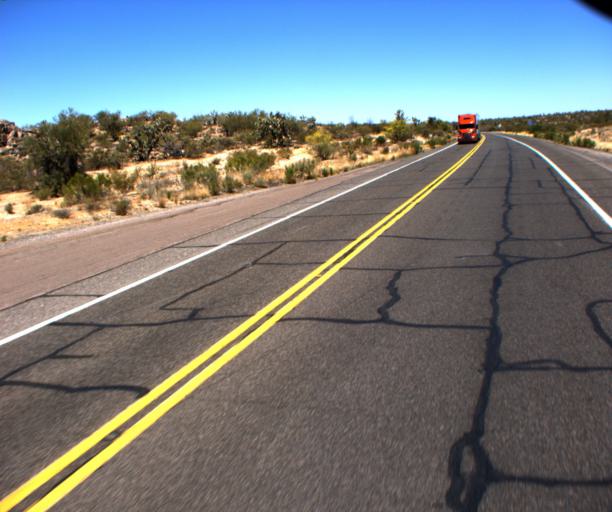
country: US
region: Arizona
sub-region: Yavapai County
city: Congress
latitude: 34.2284
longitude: -113.0699
